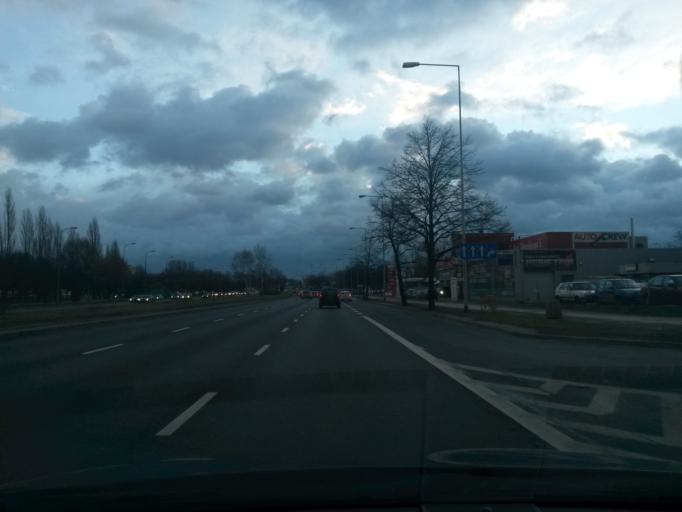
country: PL
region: Masovian Voivodeship
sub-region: Warszawa
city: Mokotow
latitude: 52.1800
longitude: 21.0446
